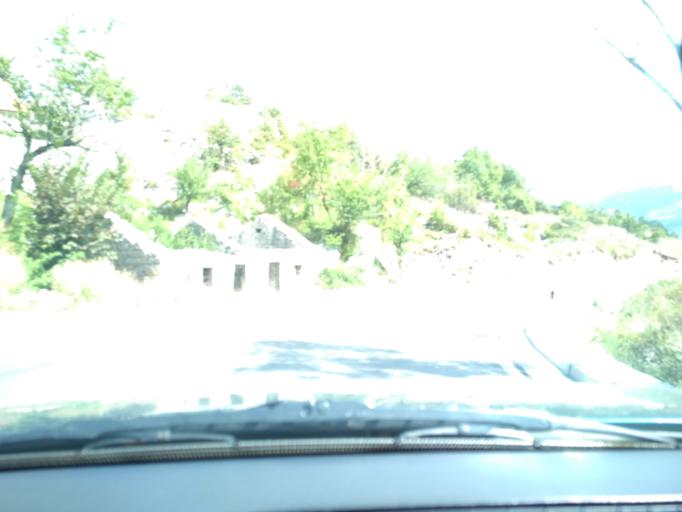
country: ME
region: Kotor
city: Kotor
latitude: 42.4327
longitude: 18.8090
